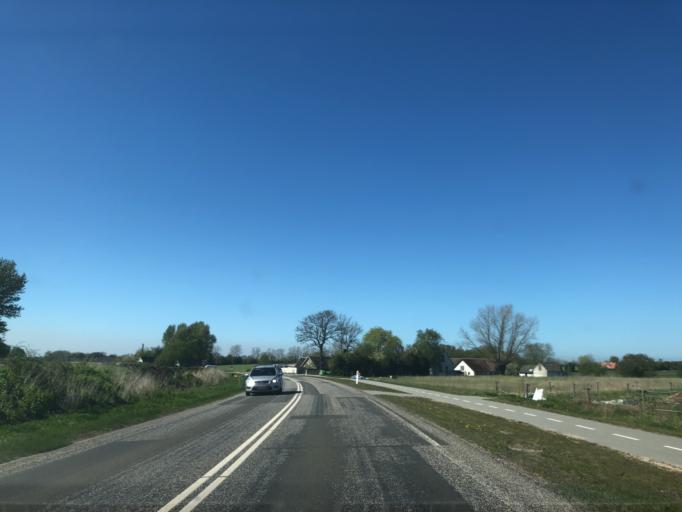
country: DK
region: Zealand
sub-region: Stevns Kommune
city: Harlev
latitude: 55.3703
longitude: 12.3010
